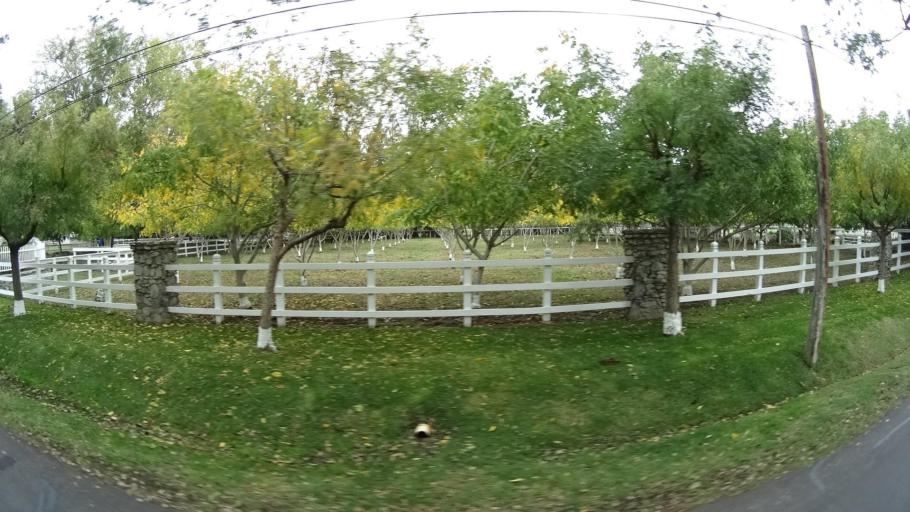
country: US
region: California
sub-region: Sacramento County
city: Wilton
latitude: 38.4331
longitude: -121.3115
